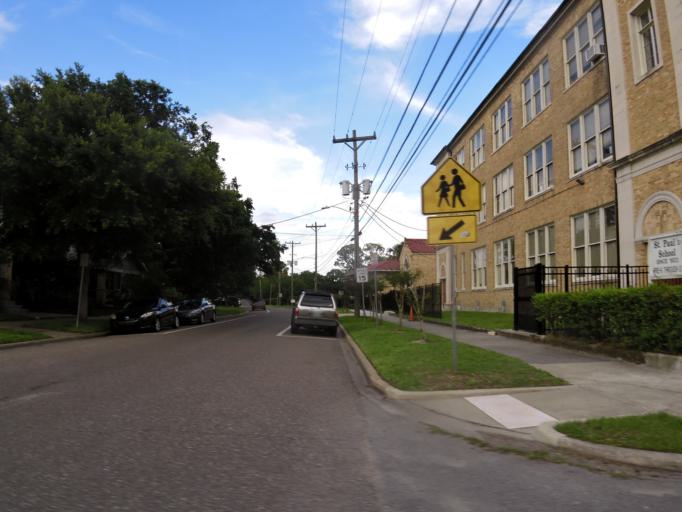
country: US
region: Florida
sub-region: Duval County
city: Jacksonville
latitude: 30.3123
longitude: -81.6927
